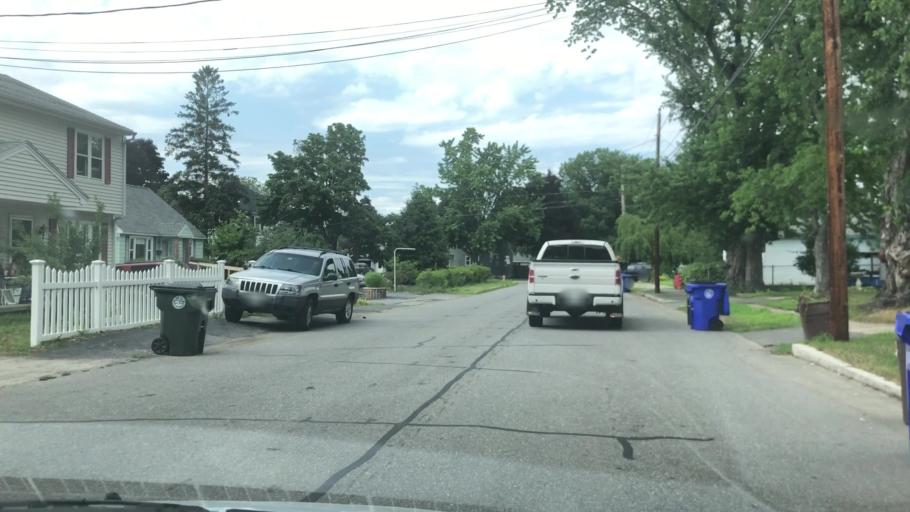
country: US
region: New Hampshire
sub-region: Hillsborough County
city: Manchester
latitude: 42.9757
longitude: -71.4331
